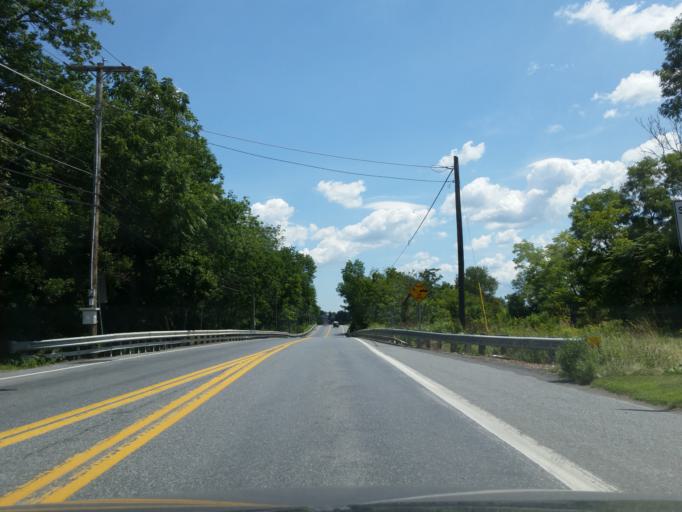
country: US
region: Pennsylvania
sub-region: Lebanon County
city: Annville
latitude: 40.3257
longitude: -76.5334
